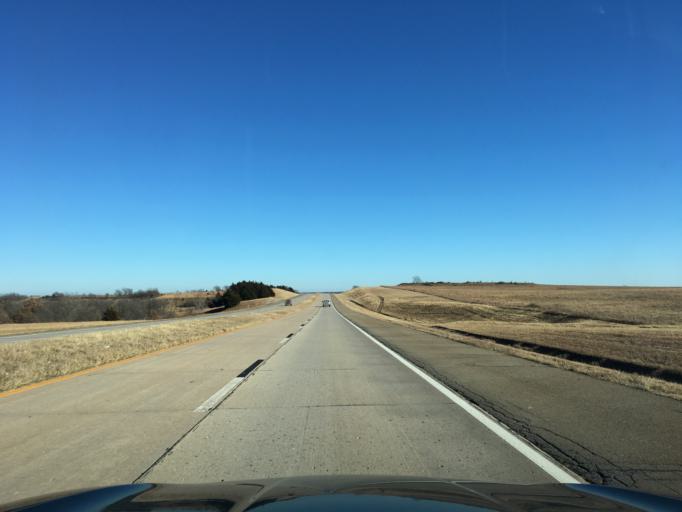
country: US
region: Oklahoma
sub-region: Payne County
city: Yale
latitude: 36.2240
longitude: -96.7386
